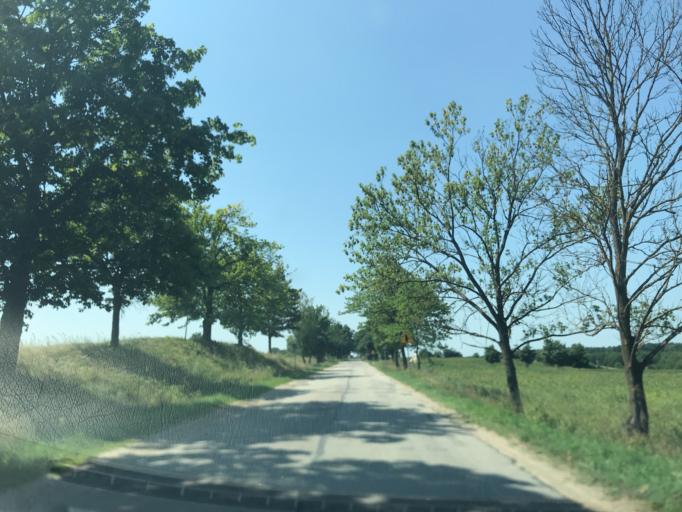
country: PL
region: Kujawsko-Pomorskie
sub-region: Powiat lipnowski
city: Chrostkowo
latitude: 52.9898
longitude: 19.2829
